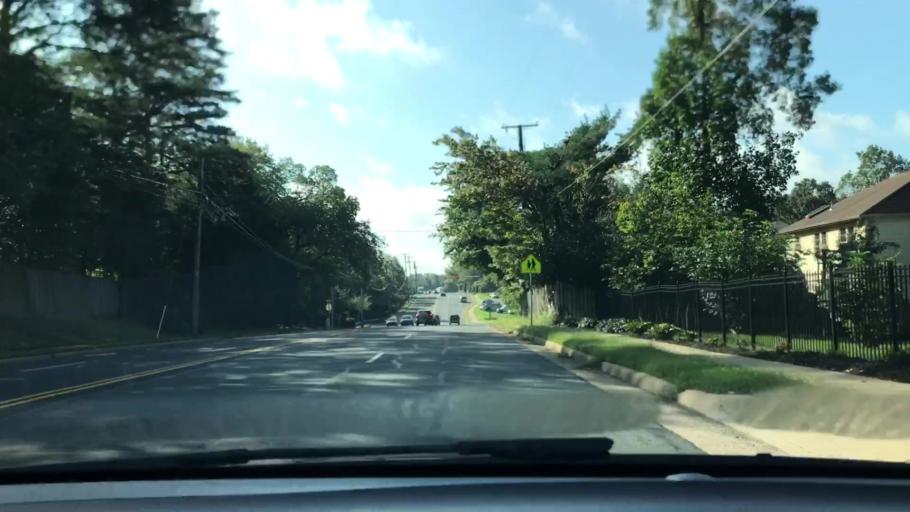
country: US
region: Virginia
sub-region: Fairfax County
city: Annandale
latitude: 38.8360
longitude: -77.1980
